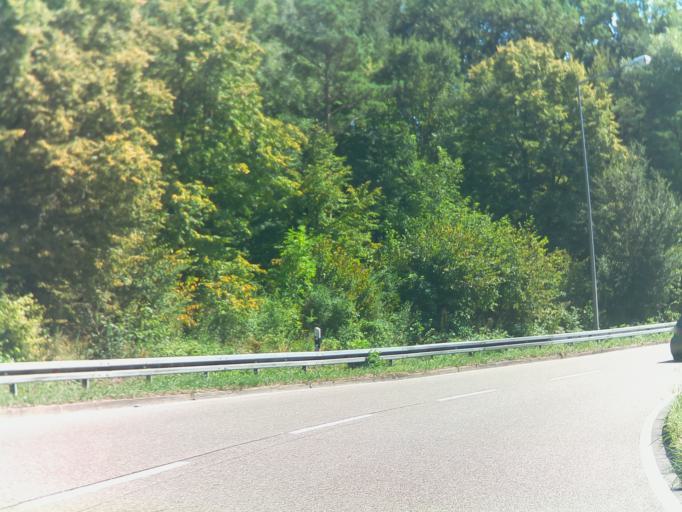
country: DE
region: Baden-Wuerttemberg
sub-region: Regierungsbezirk Stuttgart
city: Stuttgart Feuerbach
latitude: 48.7647
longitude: 9.1189
